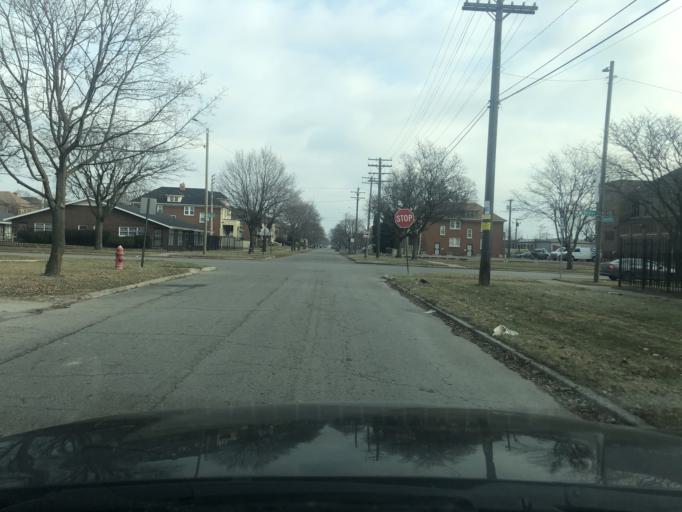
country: US
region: Michigan
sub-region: Wayne County
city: Highland Park
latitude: 42.3904
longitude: -83.1318
